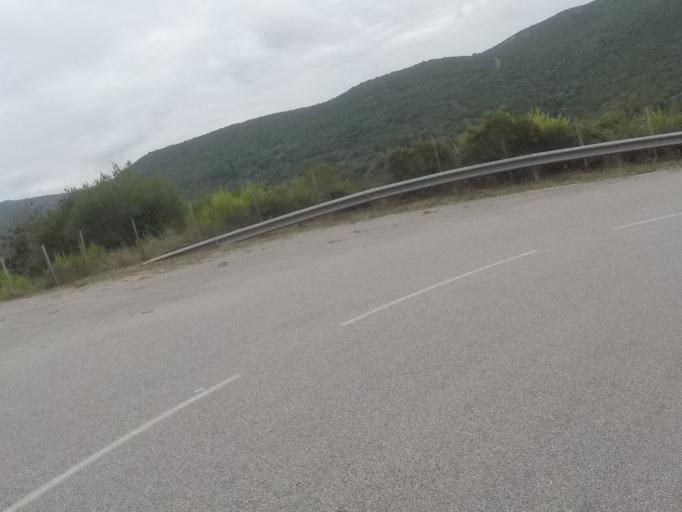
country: FR
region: Corsica
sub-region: Departement de la Corse-du-Sud
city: Pietrosella
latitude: 41.7936
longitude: 8.8256
